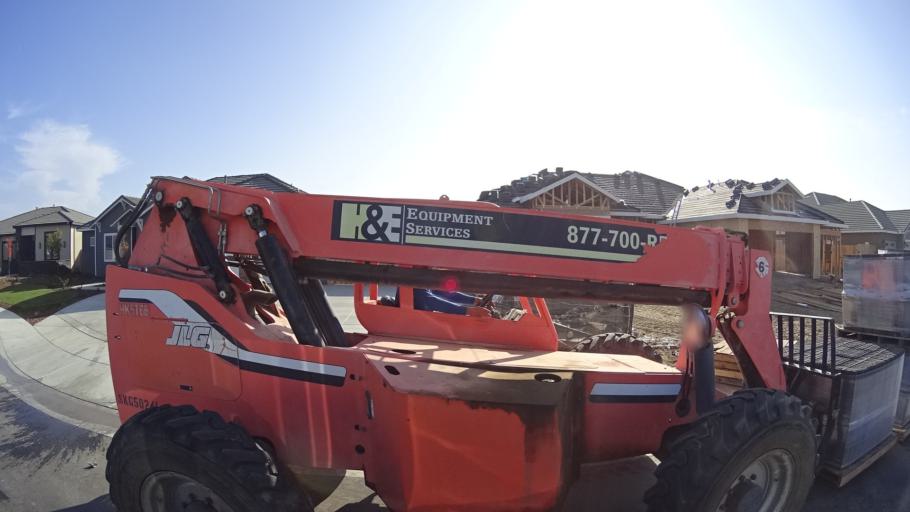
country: US
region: California
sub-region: Kern County
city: Rosedale
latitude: 35.3476
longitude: -119.1781
